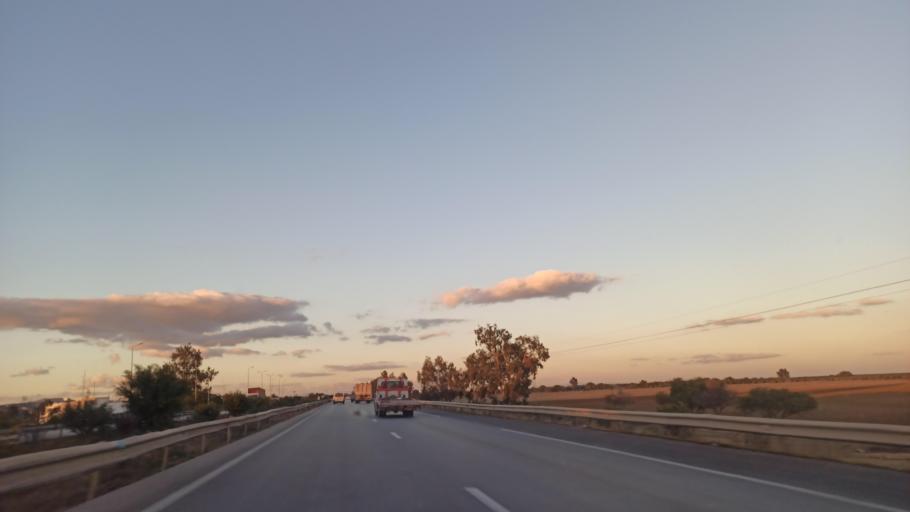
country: TN
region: Susah
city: Harqalah
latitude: 36.1286
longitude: 10.4067
